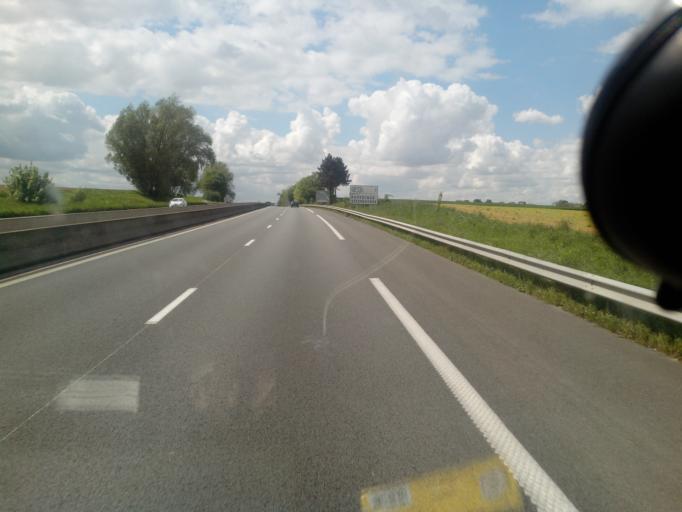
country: FR
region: Nord-Pas-de-Calais
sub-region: Departement du Nord
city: Meteren
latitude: 50.7505
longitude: 2.6660
